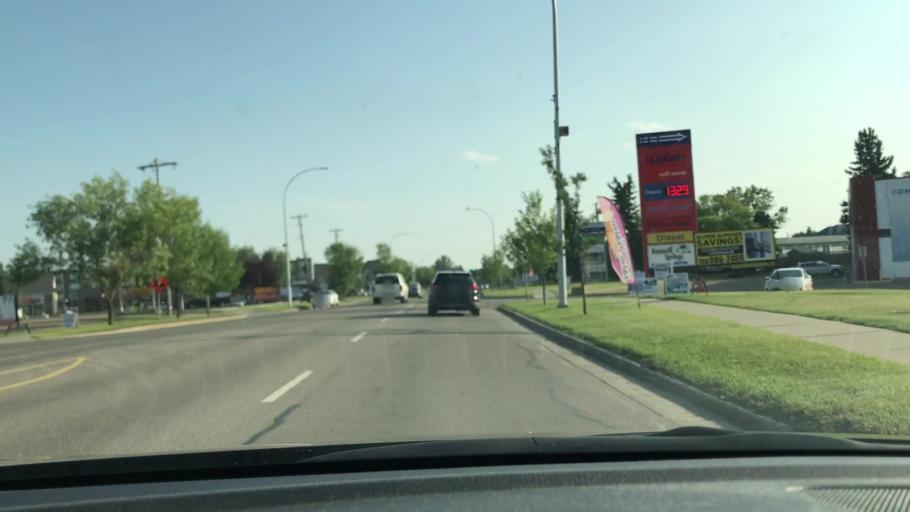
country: CA
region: Alberta
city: Leduc
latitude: 53.2735
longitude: -113.5500
